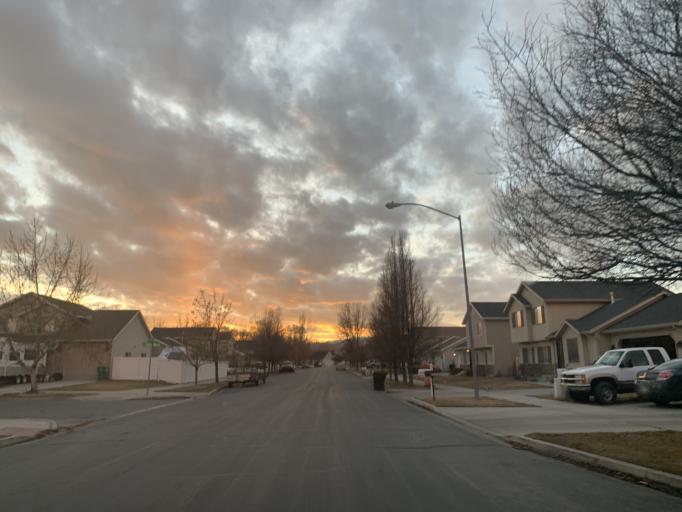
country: US
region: Utah
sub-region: Utah County
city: Provo
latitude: 40.2398
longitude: -111.7082
